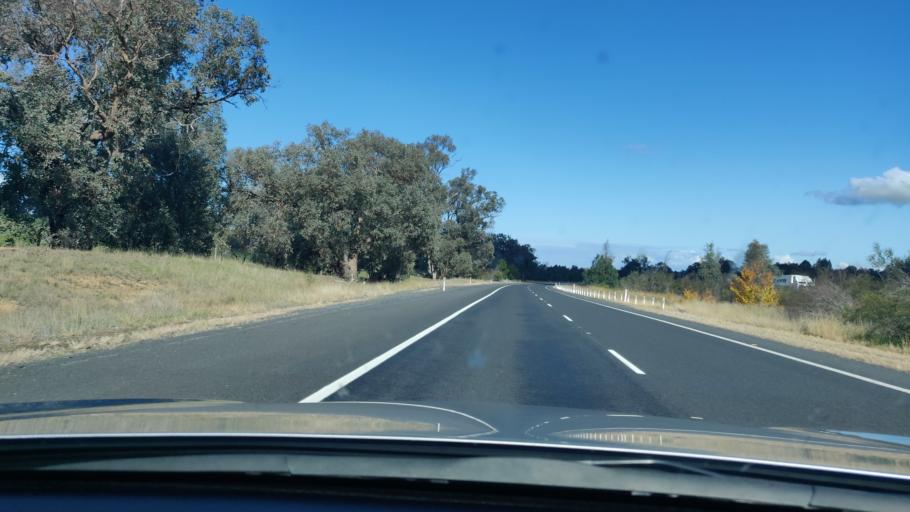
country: AU
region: New South Wales
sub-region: Greater Hume Shire
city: Holbrook
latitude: -35.8888
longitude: 147.1735
